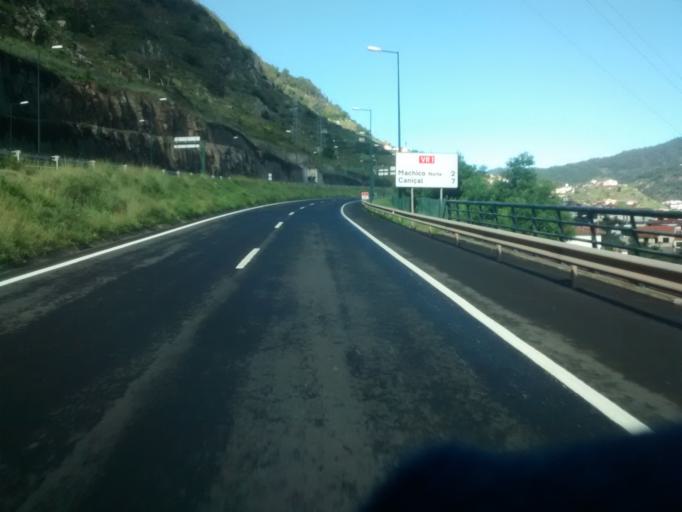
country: PT
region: Madeira
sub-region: Machico
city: Machico
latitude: 32.7170
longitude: -16.7695
